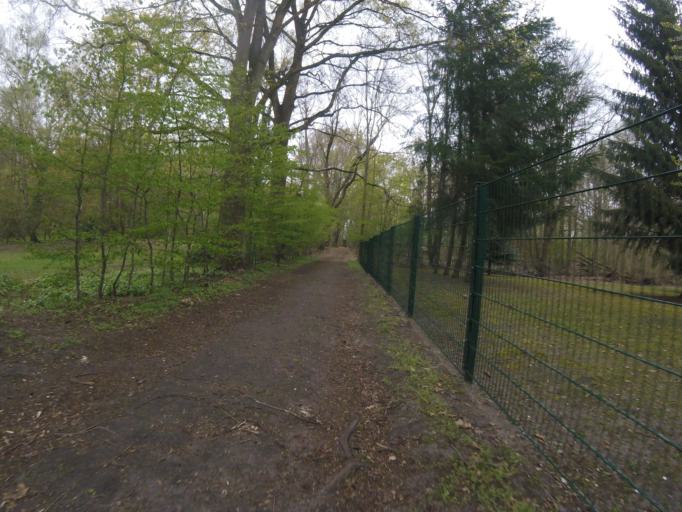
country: DE
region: Brandenburg
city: Bestensee
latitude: 52.2274
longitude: 13.6569
